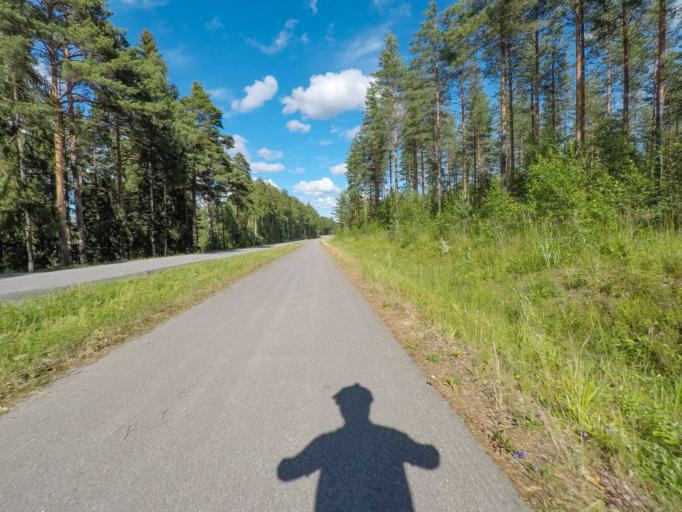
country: FI
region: South Karelia
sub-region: Lappeenranta
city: Joutseno
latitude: 61.1516
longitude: 28.5623
